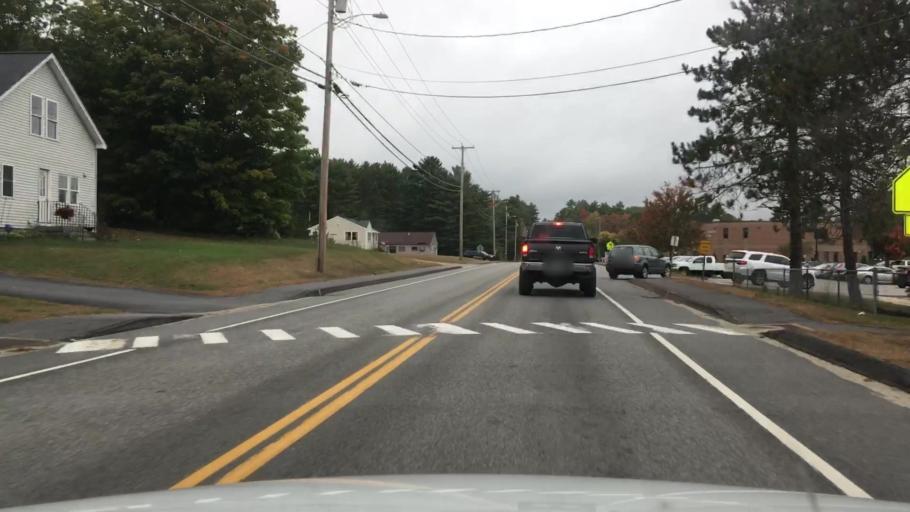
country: US
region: Maine
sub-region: Androscoggin County
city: Poland
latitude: 44.0628
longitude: -70.3961
